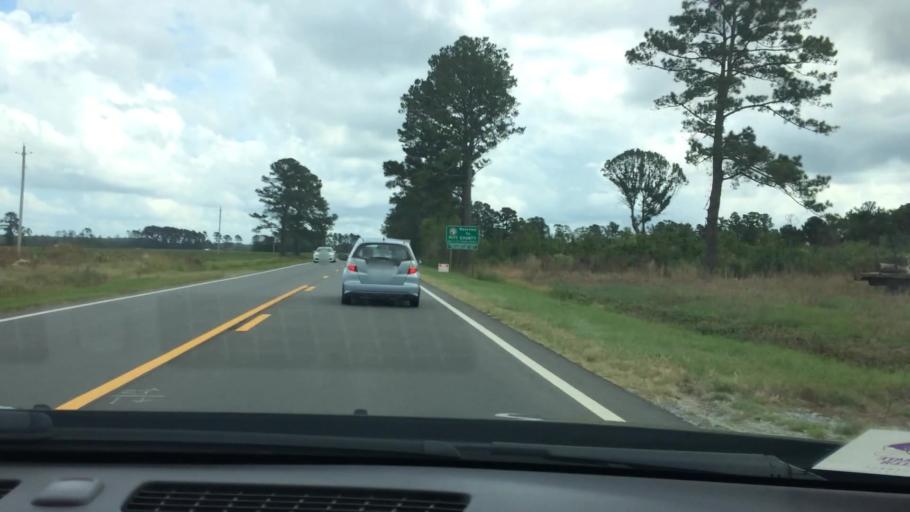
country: US
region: North Carolina
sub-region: Pitt County
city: Farmville
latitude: 35.6019
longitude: -77.6440
